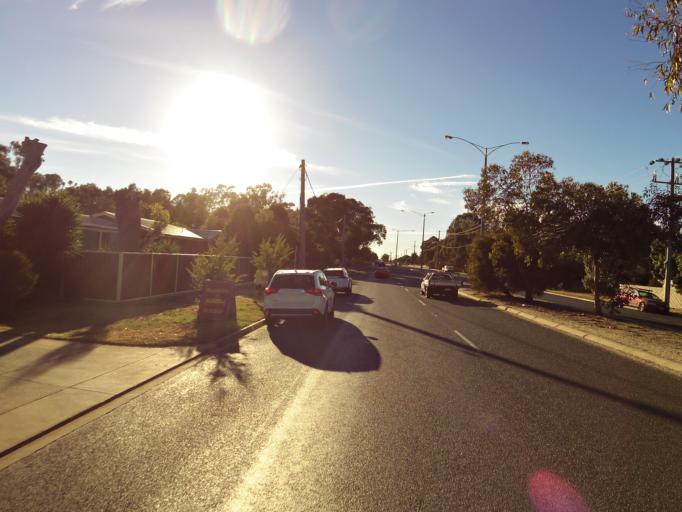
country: AU
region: Victoria
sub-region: Campaspe
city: Echuca
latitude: -36.1404
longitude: 144.7387
